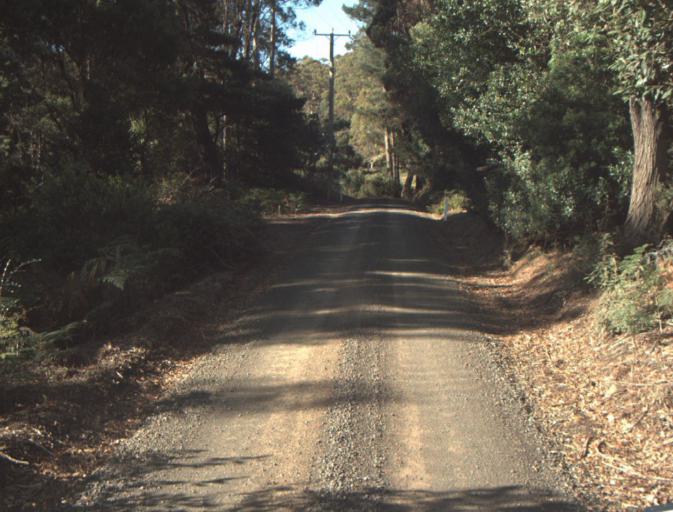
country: AU
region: Tasmania
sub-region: Launceston
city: Mayfield
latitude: -41.3021
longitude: 147.1983
